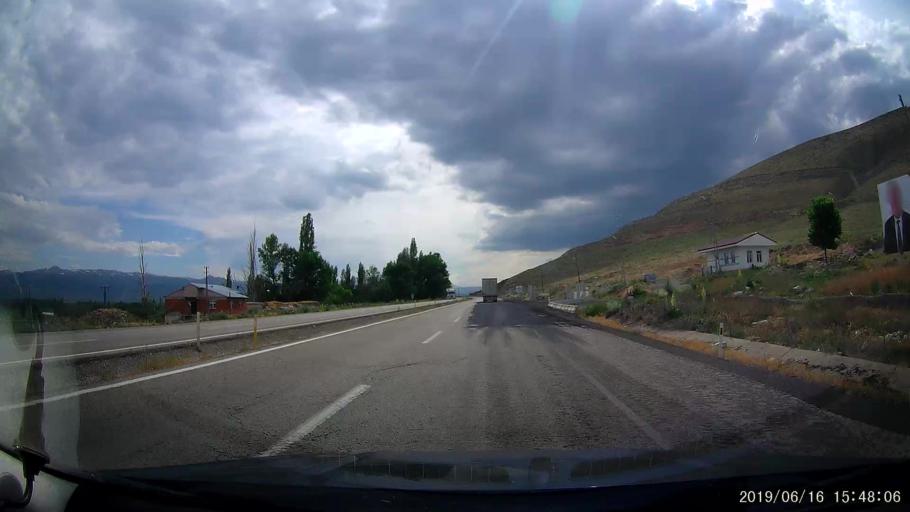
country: TR
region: Erzurum
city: Pasinler
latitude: 39.9854
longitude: 41.7081
